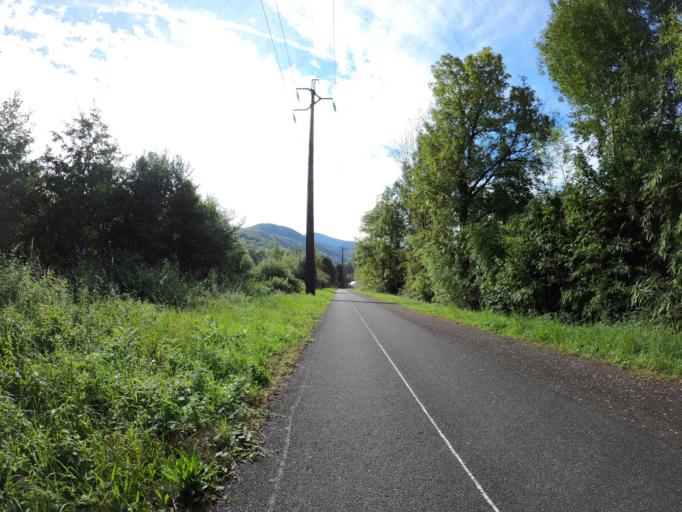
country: FR
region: Midi-Pyrenees
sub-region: Departement des Hautes-Pyrenees
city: Lourdes
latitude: 43.0677
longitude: -0.0404
